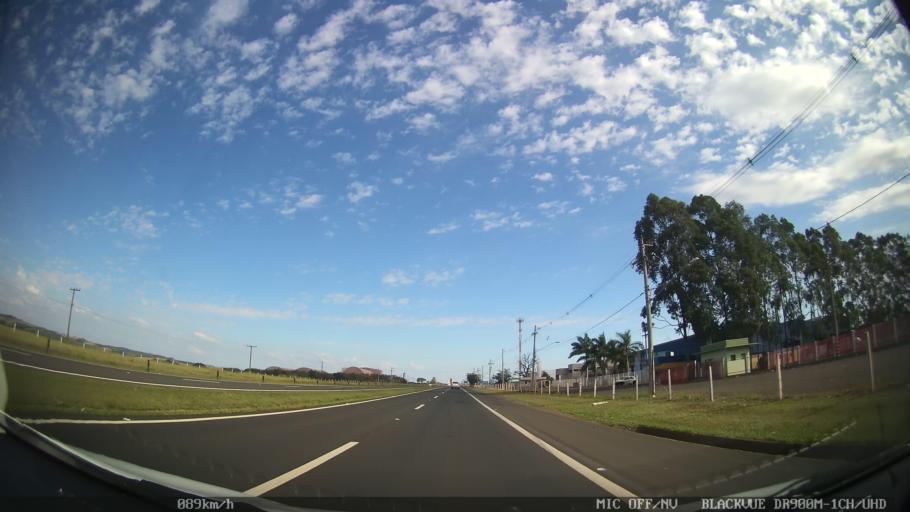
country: BR
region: Sao Paulo
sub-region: Iracemapolis
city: Iracemapolis
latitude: -22.6074
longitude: -47.4761
